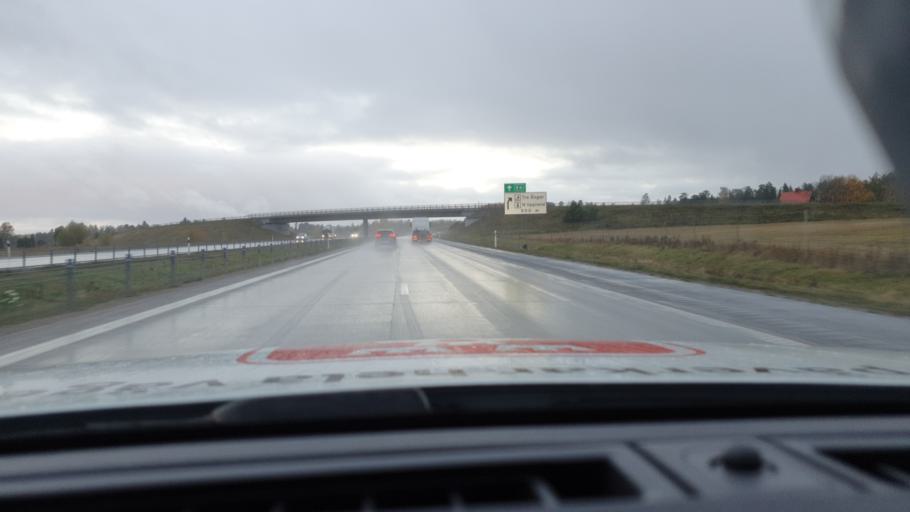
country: SE
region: Uppsala
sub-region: Uppsala Kommun
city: Storvreta
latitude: 59.9779
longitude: 17.6428
